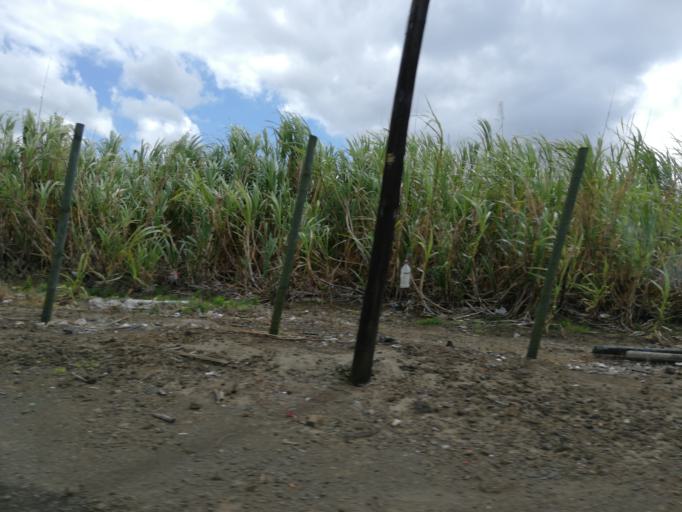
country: MU
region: Riviere du Rempart
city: Esperance Trebuchet
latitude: -20.0731
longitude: 57.6639
